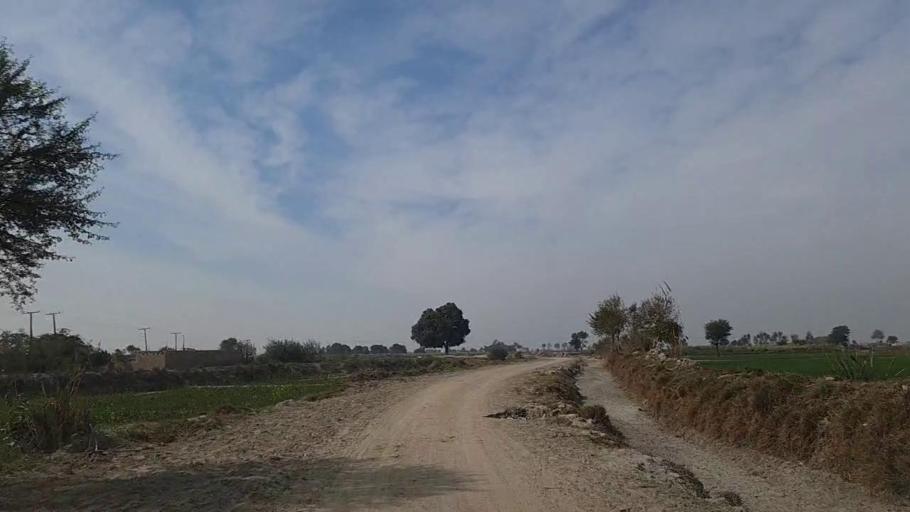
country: PK
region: Sindh
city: Nawabshah
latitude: 26.3281
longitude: 68.4211
